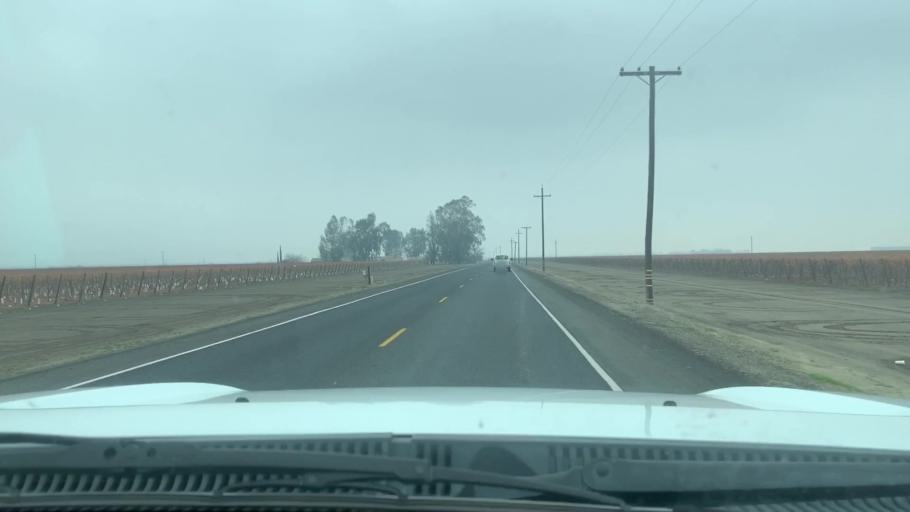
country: US
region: California
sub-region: Kern County
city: Buttonwillow
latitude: 35.4994
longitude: -119.5869
